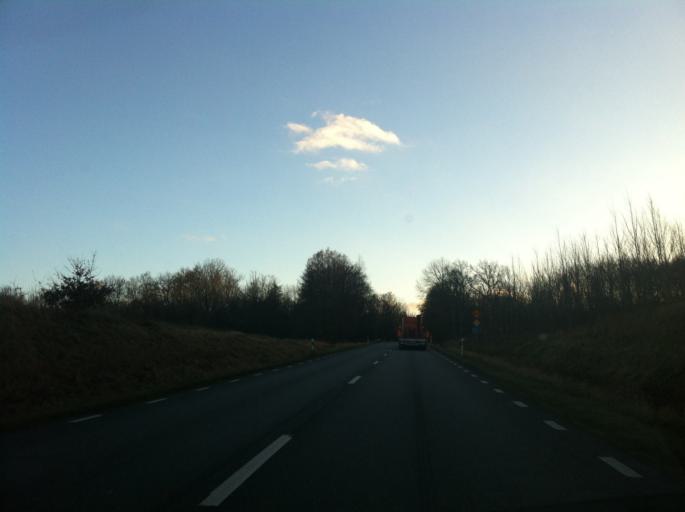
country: SE
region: Skane
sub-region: Hassleholms Kommun
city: Hassleholm
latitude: 56.1830
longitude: 13.8507
